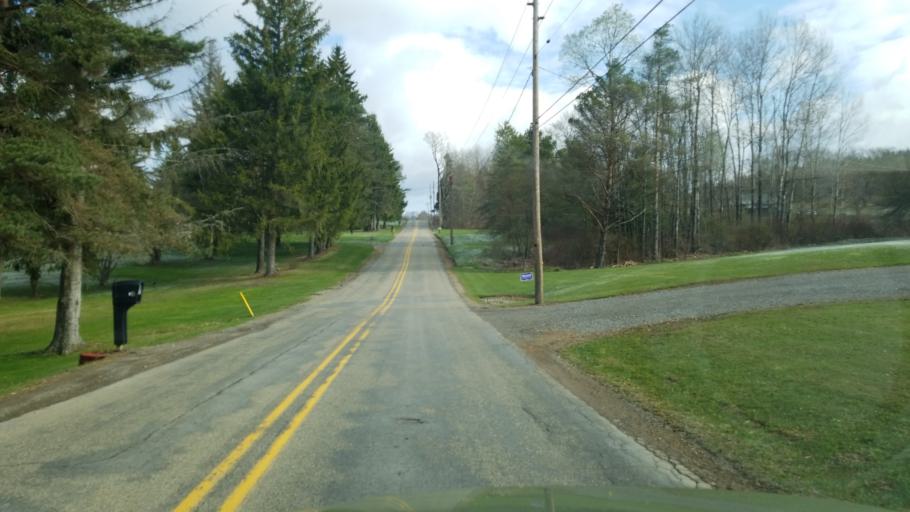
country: US
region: Pennsylvania
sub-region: Jefferson County
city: Brockway
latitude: 41.2577
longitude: -78.8385
